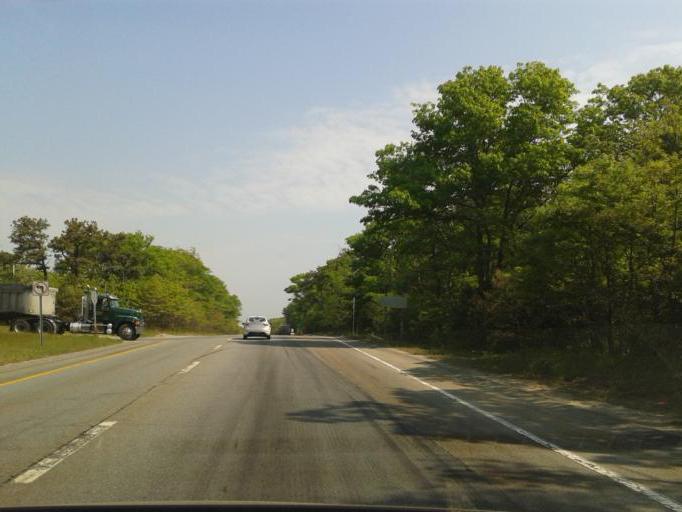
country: US
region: Massachusetts
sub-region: Barnstable County
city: Bourne
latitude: 41.7293
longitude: -70.5841
